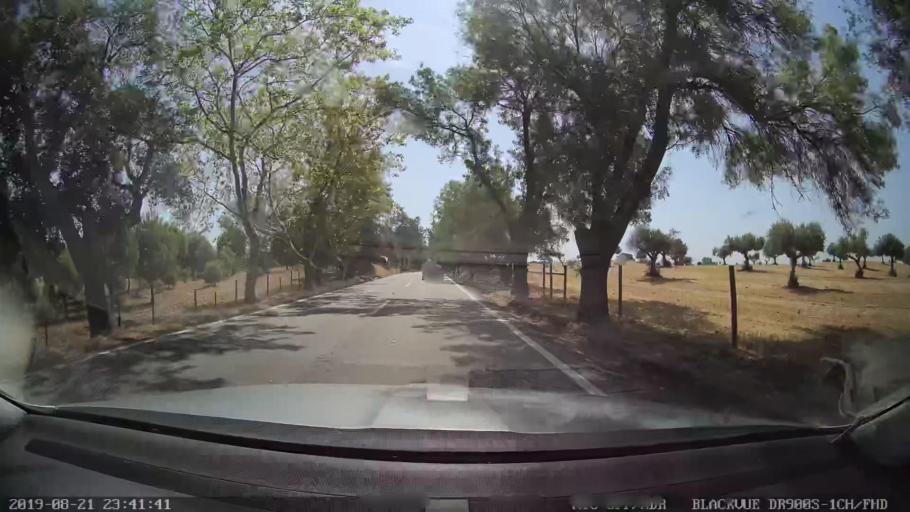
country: PT
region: Castelo Branco
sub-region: Idanha-A-Nova
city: Idanha-a-Nova
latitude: 39.8631
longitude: -7.3198
